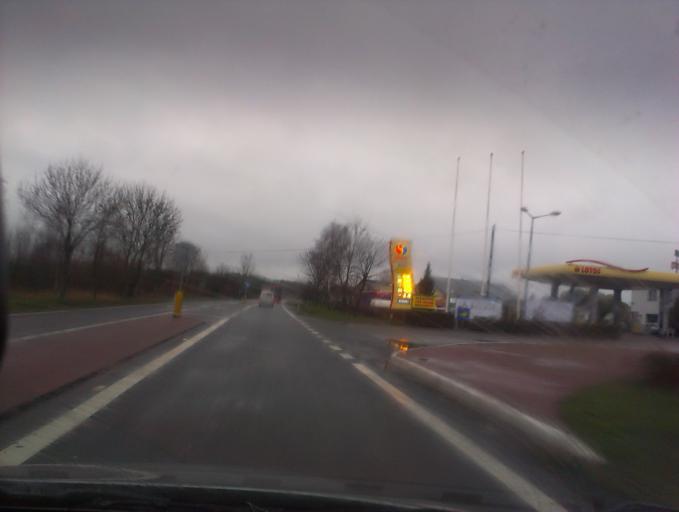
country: PL
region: Greater Poland Voivodeship
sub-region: Powiat chodzieski
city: Budzyn
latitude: 52.8993
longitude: 16.9700
